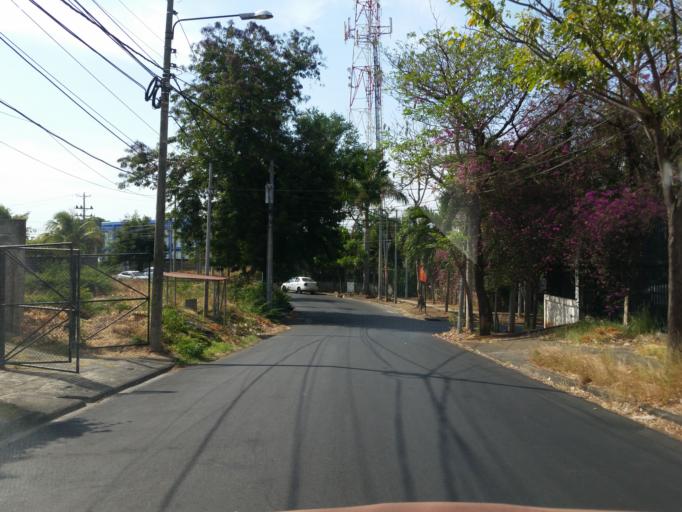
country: NI
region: Managua
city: Managua
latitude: 12.1162
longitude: -86.2637
